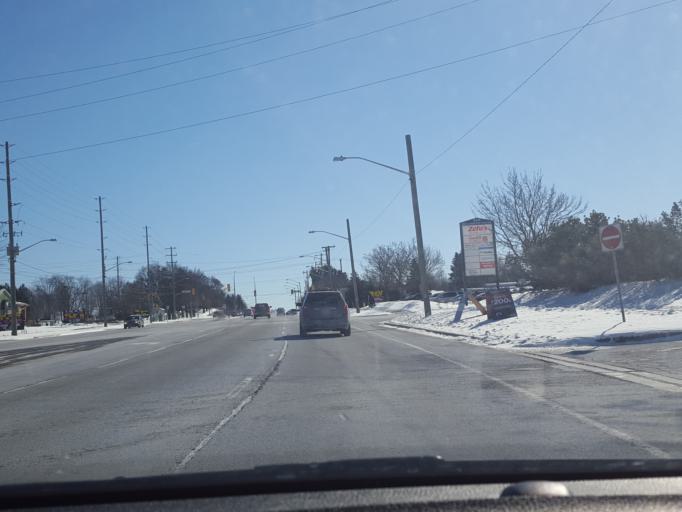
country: CA
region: Ontario
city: Waterloo
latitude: 43.4542
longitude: -80.5551
